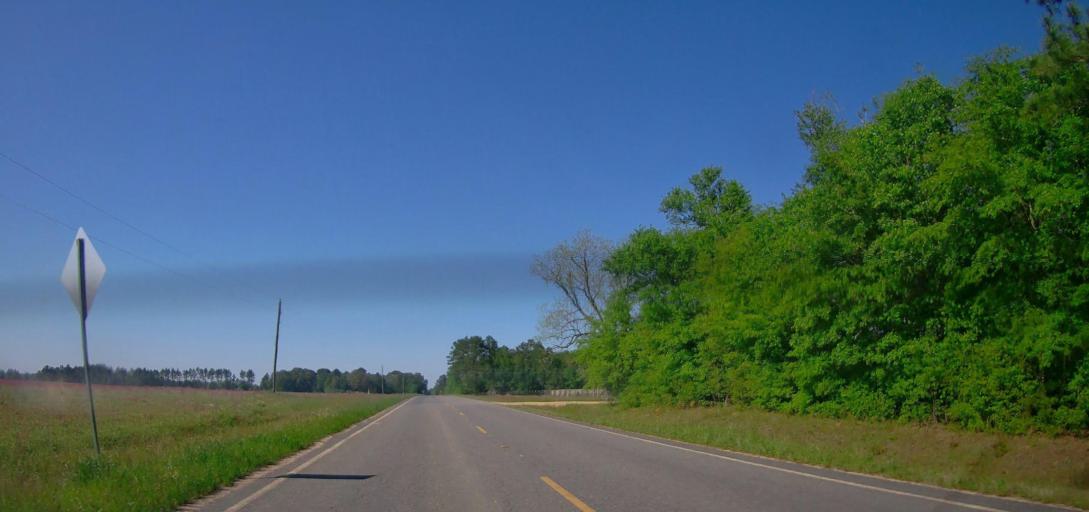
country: US
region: Georgia
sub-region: Wilcox County
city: Rochelle
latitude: 32.0788
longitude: -83.5035
